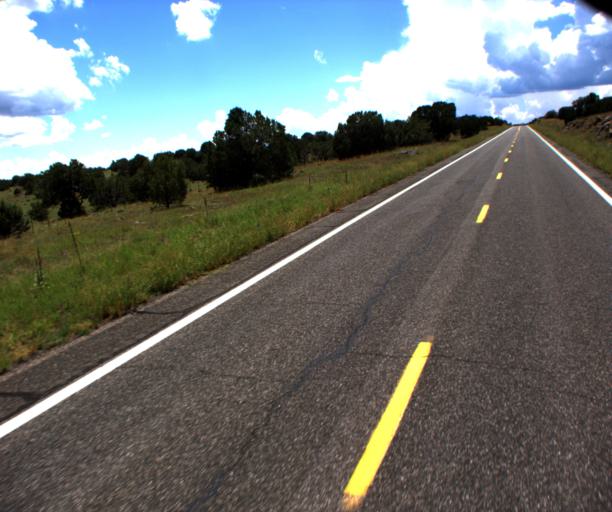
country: US
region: Arizona
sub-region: Gila County
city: Pine
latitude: 34.4953
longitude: -111.5885
